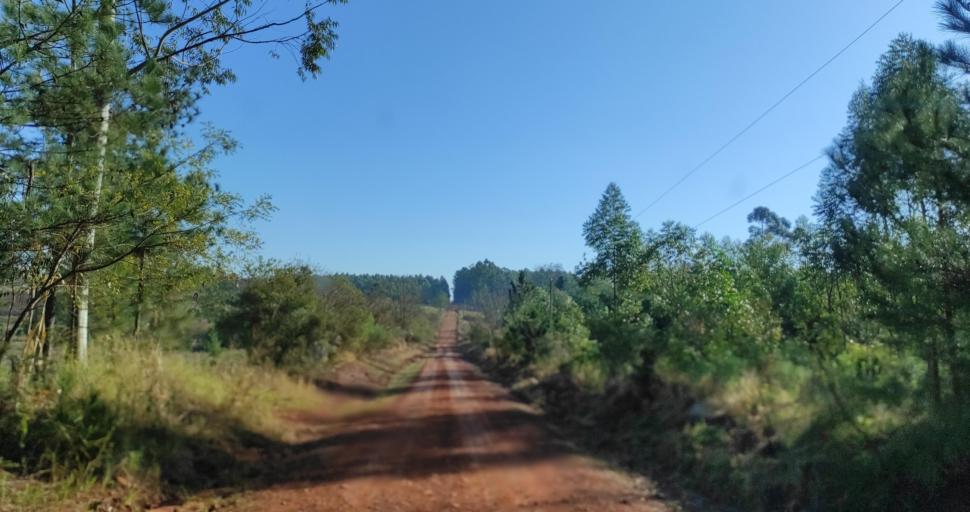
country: AR
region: Misiones
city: Capiovi
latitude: -26.8706
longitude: -55.0157
